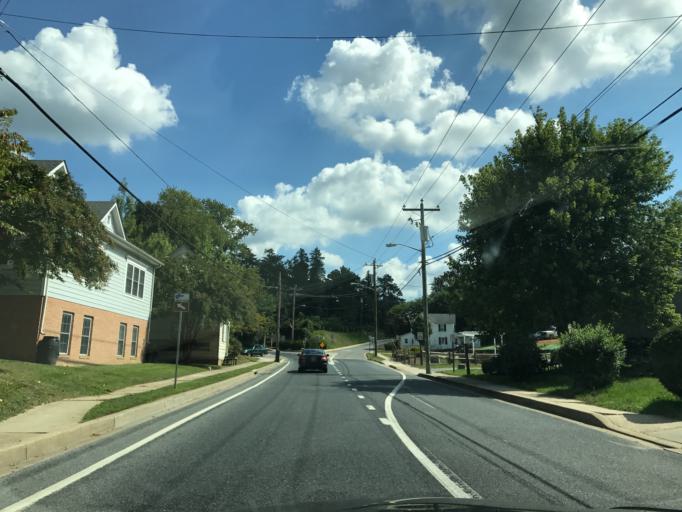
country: US
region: Maryland
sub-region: Queen Anne's County
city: Centreville
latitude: 39.0406
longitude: -76.0702
